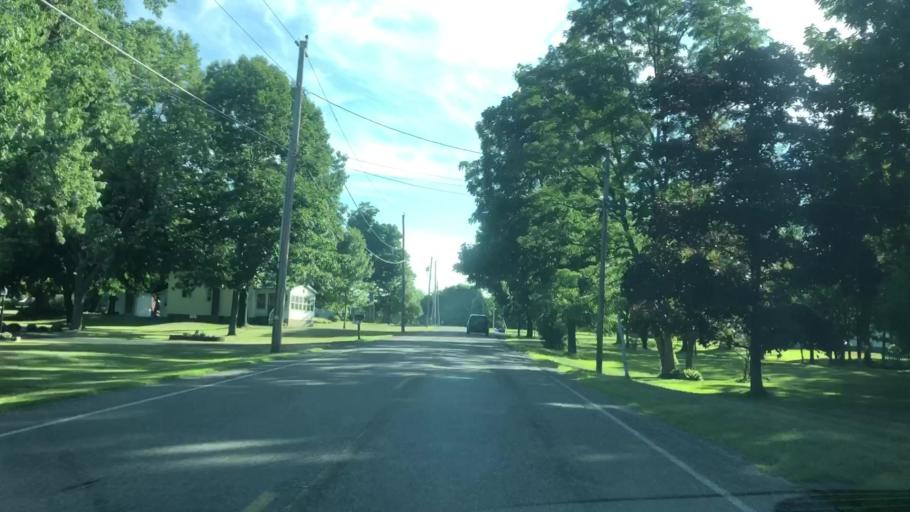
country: US
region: New York
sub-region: Wayne County
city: Macedon
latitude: 43.0508
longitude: -77.3341
